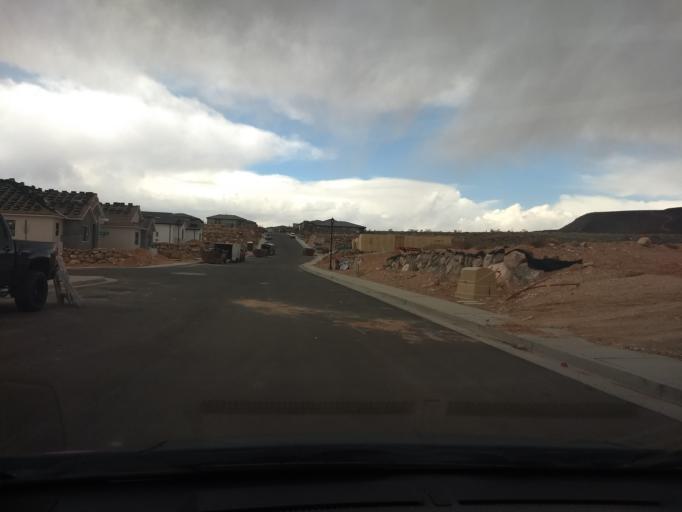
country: US
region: Utah
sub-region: Washington County
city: Washington
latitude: 37.1615
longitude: -113.5214
